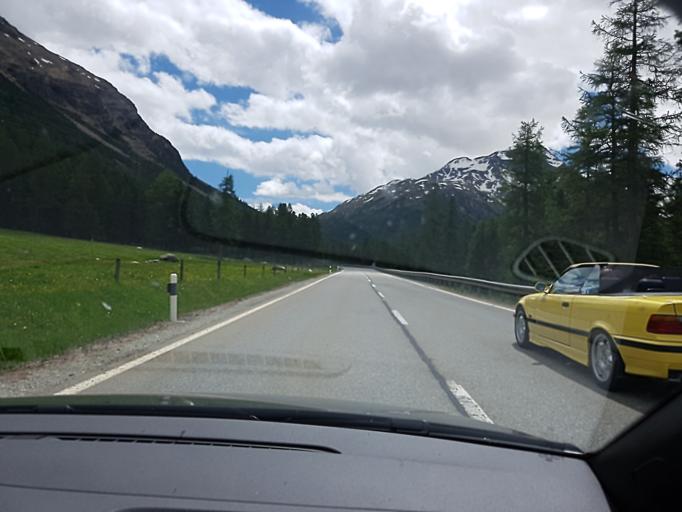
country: CH
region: Grisons
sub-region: Maloja District
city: Pontresina
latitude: 46.4677
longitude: 9.9298
